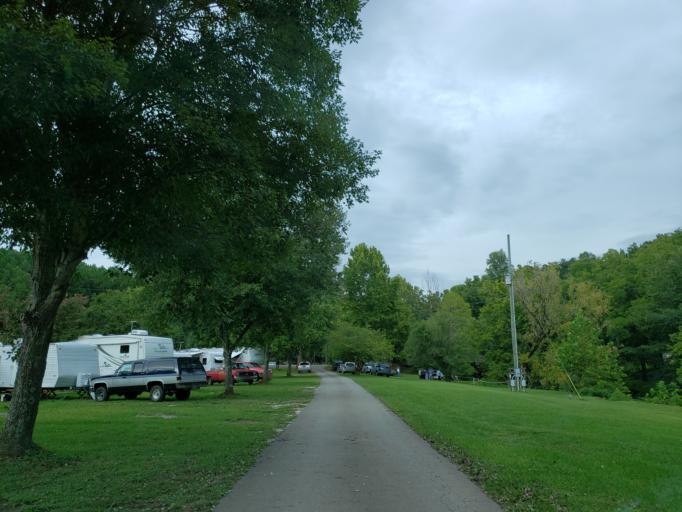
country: US
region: Georgia
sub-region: Pickens County
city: Jasper
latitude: 34.5257
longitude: -84.5101
